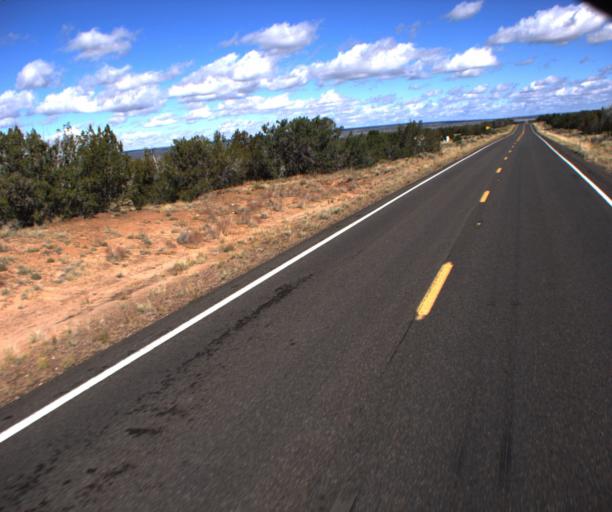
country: US
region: Arizona
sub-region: Apache County
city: Saint Johns
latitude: 34.8428
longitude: -109.2376
